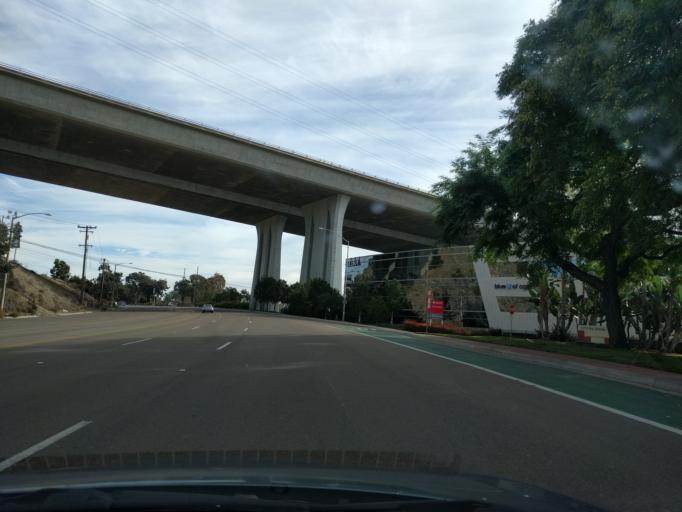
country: US
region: California
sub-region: San Diego County
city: San Diego
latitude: 32.7776
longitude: -117.1377
